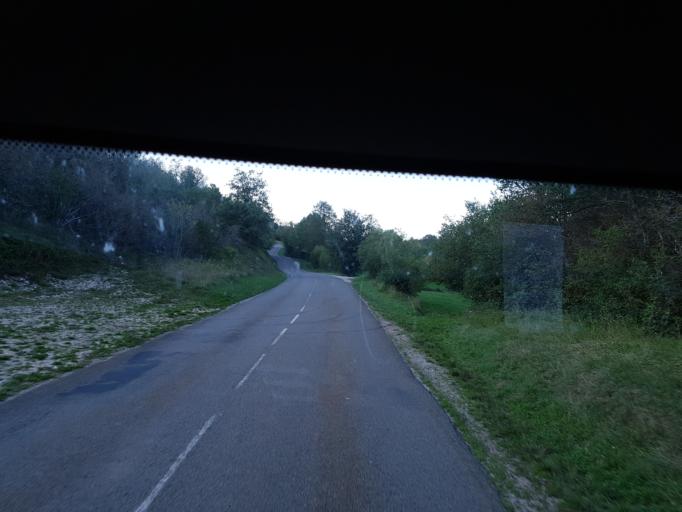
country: FR
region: Franche-Comte
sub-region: Departement du Jura
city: Moirans-en-Montagne
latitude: 46.4111
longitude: 5.6488
